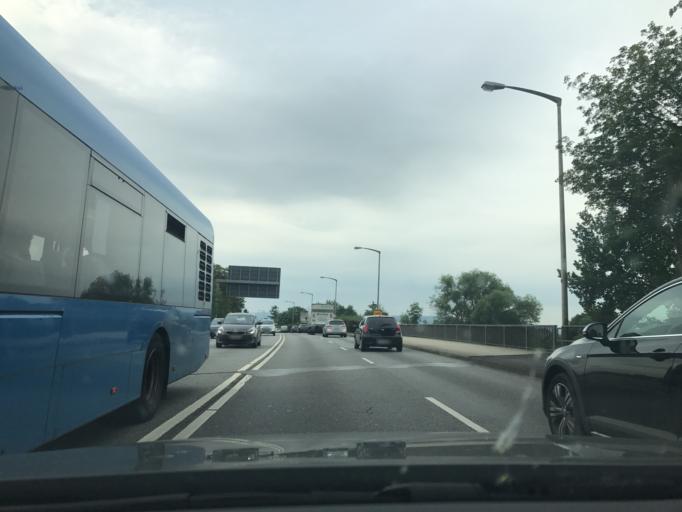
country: DE
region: Hesse
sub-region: Regierungsbezirk Kassel
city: Kassel
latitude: 51.3079
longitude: 9.5128
